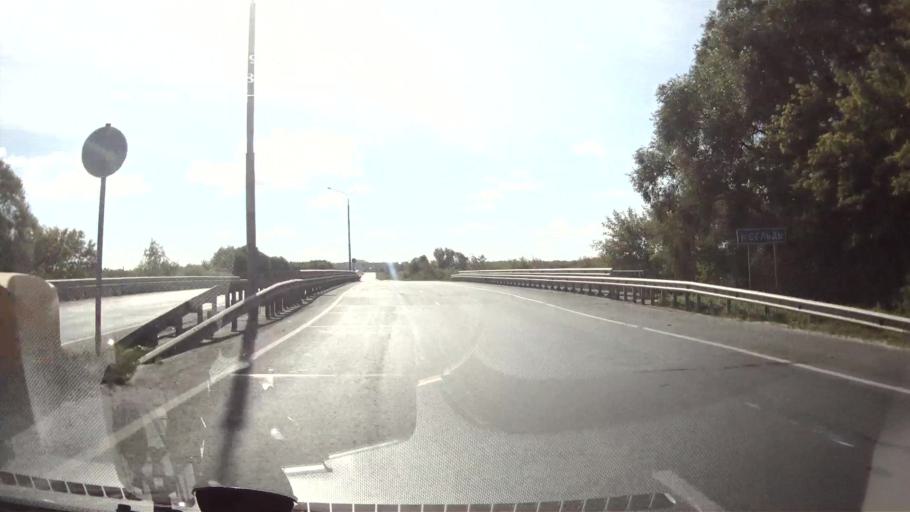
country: RU
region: Ulyanovsk
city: Isheyevka
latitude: 54.3042
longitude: 48.2416
